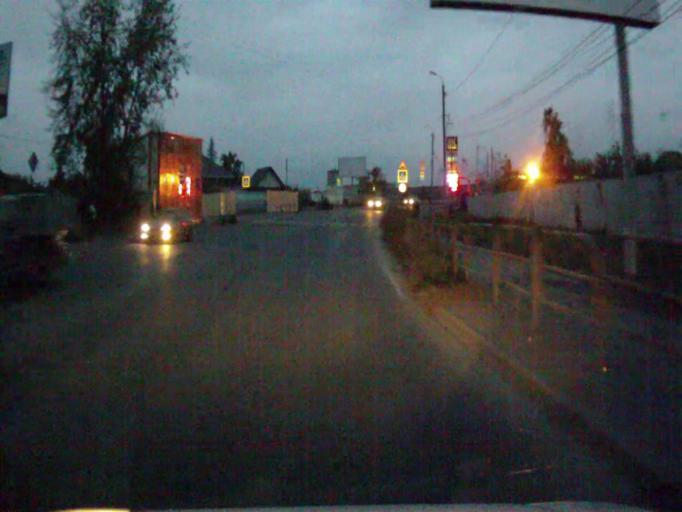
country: RU
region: Chelyabinsk
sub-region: Gorod Chelyabinsk
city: Chelyabinsk
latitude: 55.1531
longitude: 61.3033
